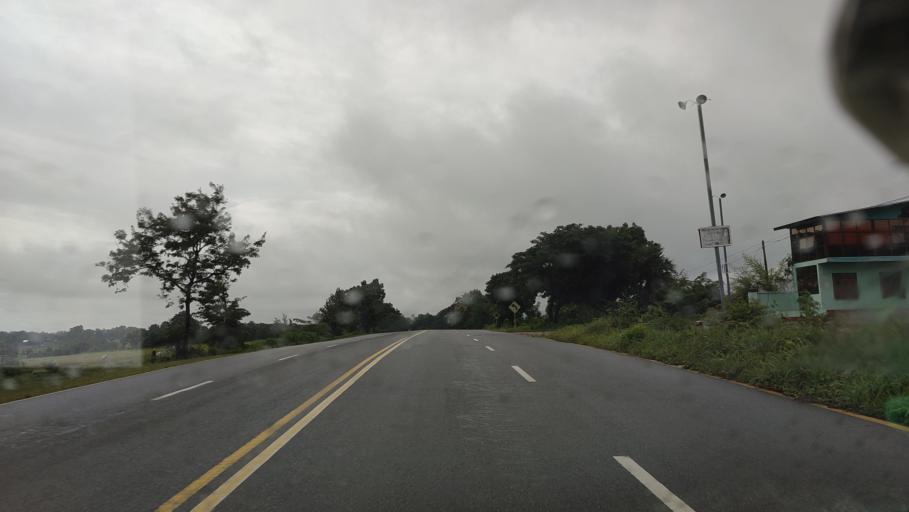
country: MM
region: Mandalay
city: Pyinmana
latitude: 19.9512
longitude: 96.2541
